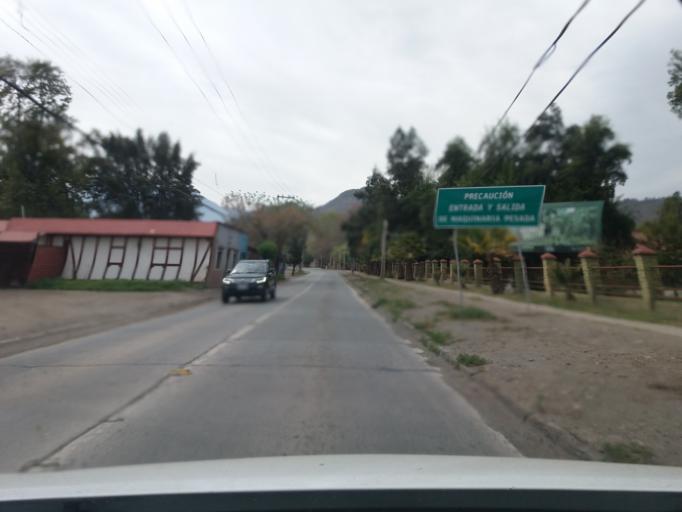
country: CL
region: Valparaiso
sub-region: Provincia de Los Andes
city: Los Andes
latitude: -32.8372
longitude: -70.5807
